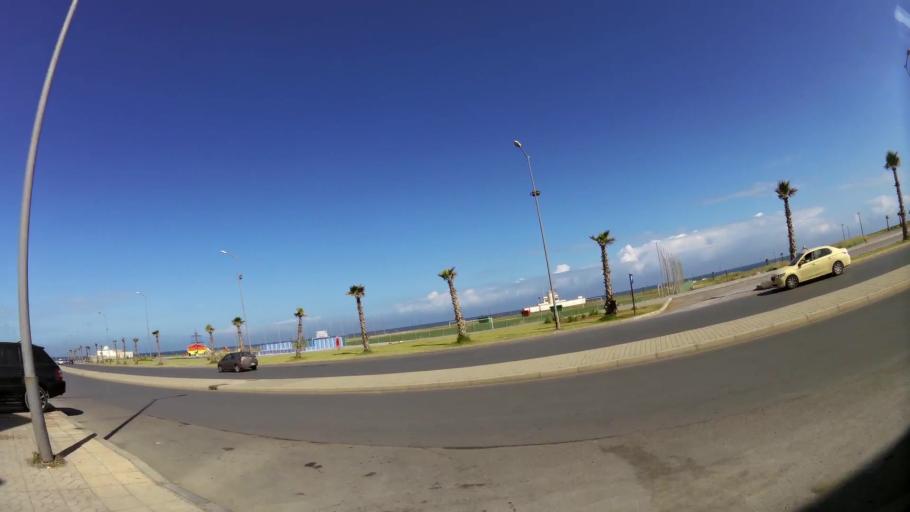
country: MA
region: Rabat-Sale-Zemmour-Zaer
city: Sale
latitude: 34.0604
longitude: -6.8142
